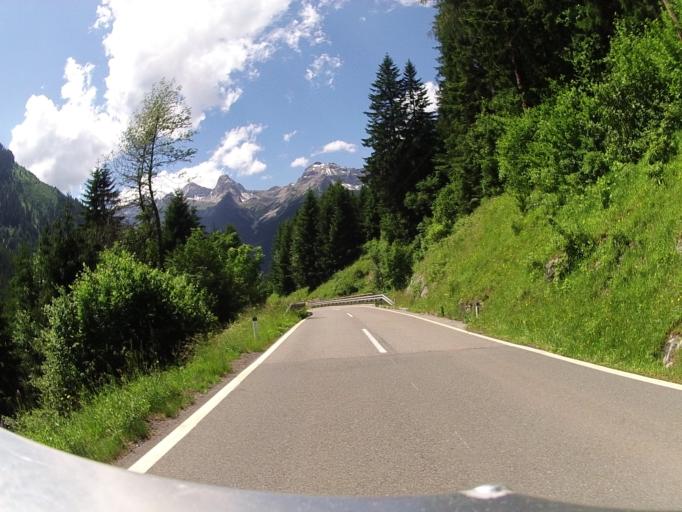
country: AT
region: Tyrol
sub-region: Politischer Bezirk Reutte
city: Elmen
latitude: 47.3184
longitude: 10.5517
